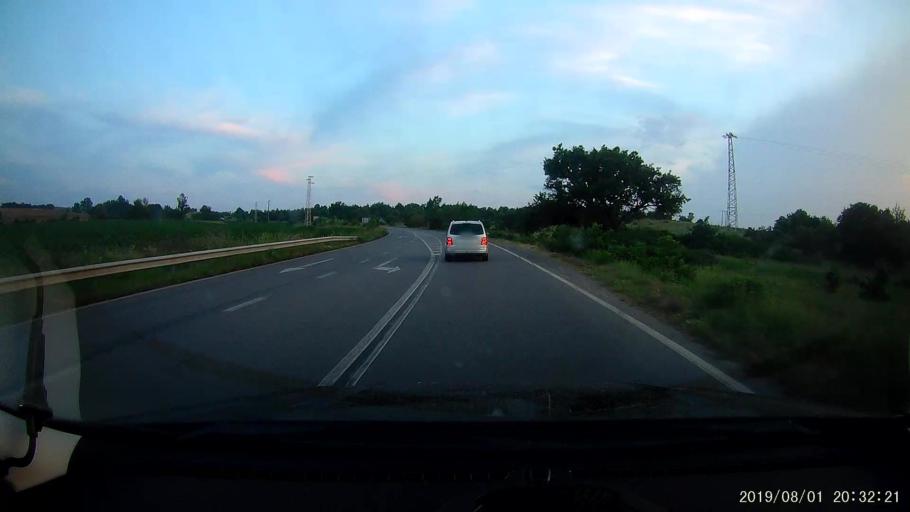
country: BG
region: Yambol
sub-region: Obshtina Elkhovo
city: Elkhovo
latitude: 42.1231
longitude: 26.5309
